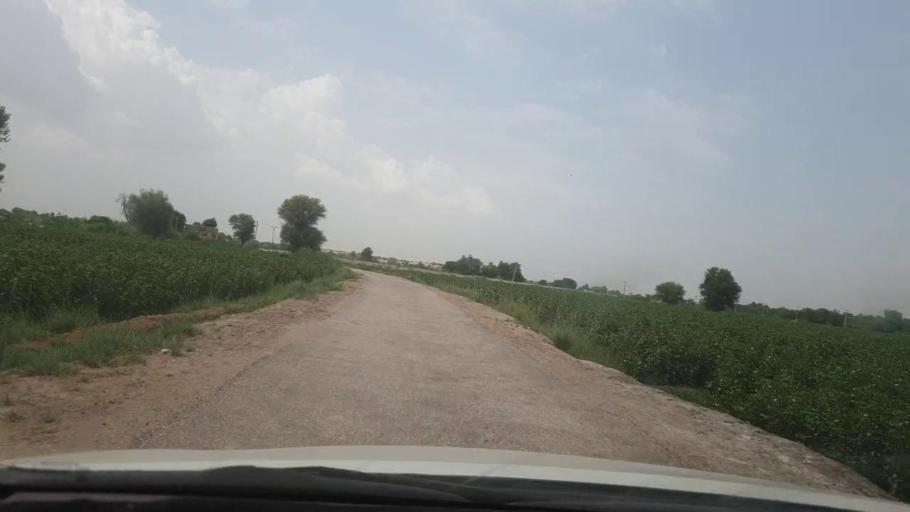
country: PK
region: Sindh
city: Kot Diji
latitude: 27.3095
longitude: 69.0123
